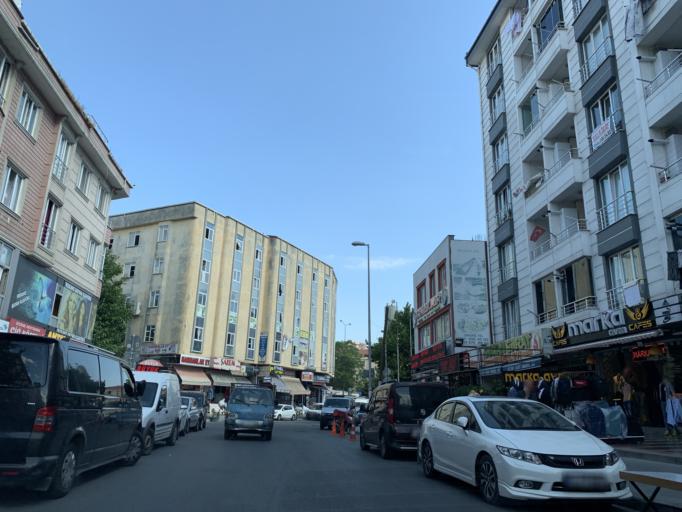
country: TR
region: Istanbul
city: Esenyurt
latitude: 41.0346
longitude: 28.6769
